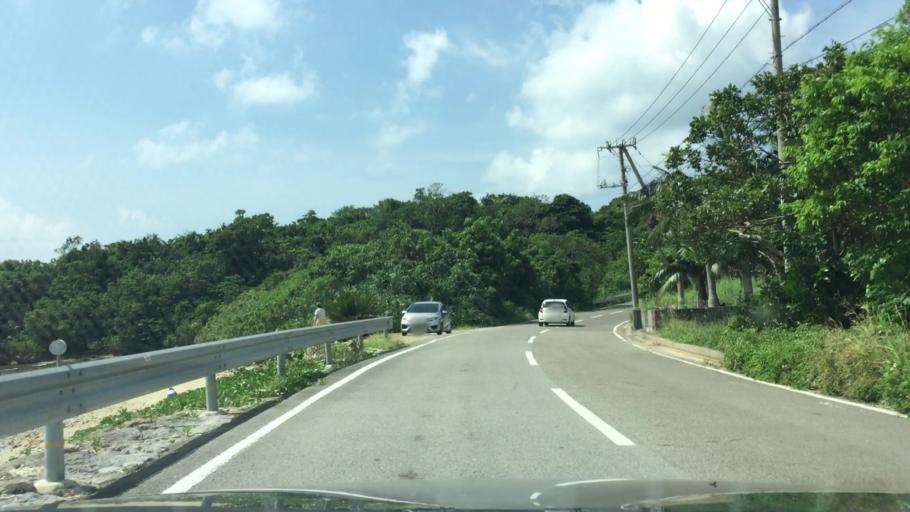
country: JP
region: Okinawa
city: Ishigaki
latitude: 24.4669
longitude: 124.2258
